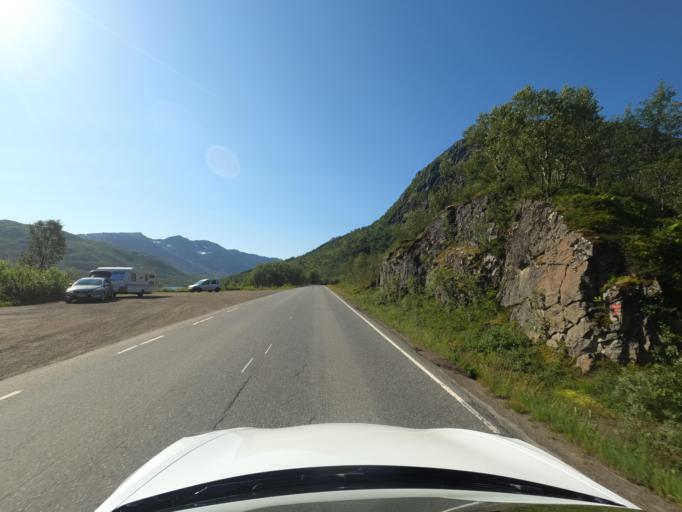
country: NO
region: Nordland
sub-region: Lodingen
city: Lodingen
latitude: 68.5599
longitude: 15.7509
